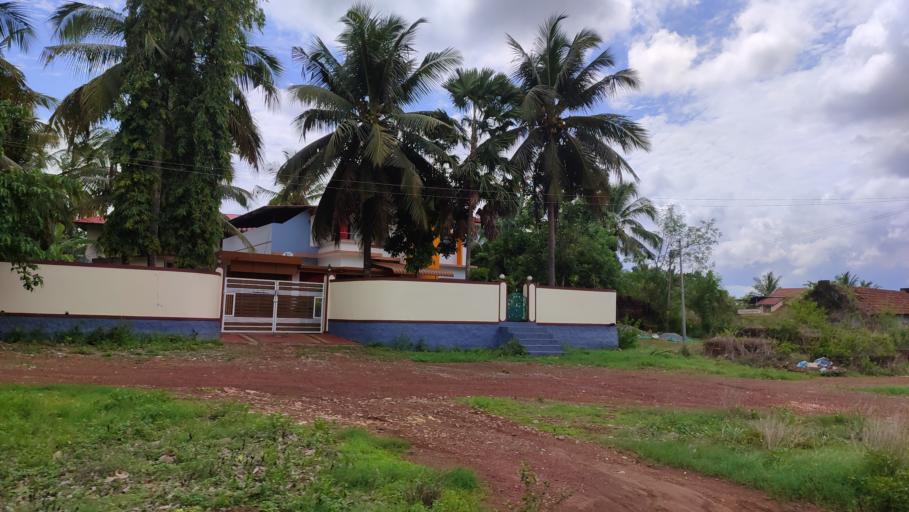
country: IN
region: Kerala
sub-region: Kasaragod District
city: Kannangad
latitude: 12.3995
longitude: 75.0973
